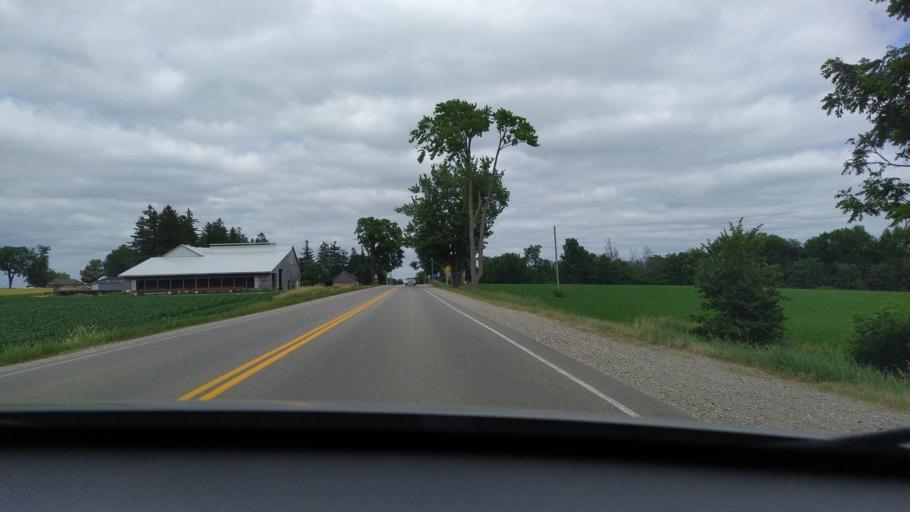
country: CA
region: Ontario
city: Stratford
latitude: 43.3157
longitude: -80.9563
